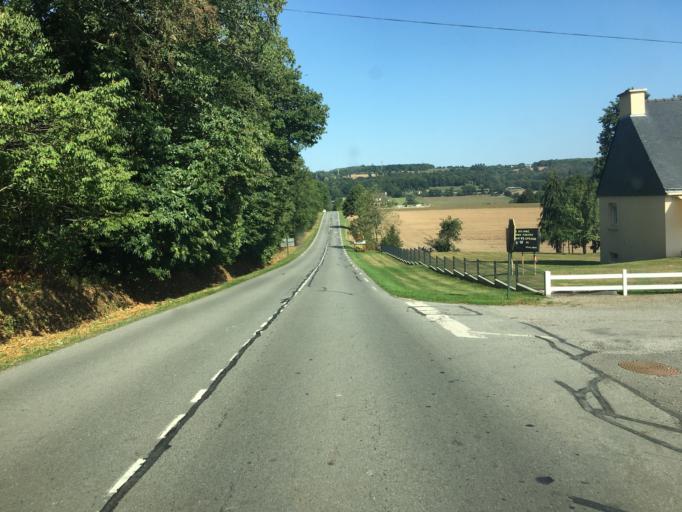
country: FR
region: Brittany
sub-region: Departement des Cotes-d'Armor
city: Mur-de-Bretagne
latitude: 48.2042
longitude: -2.9913
